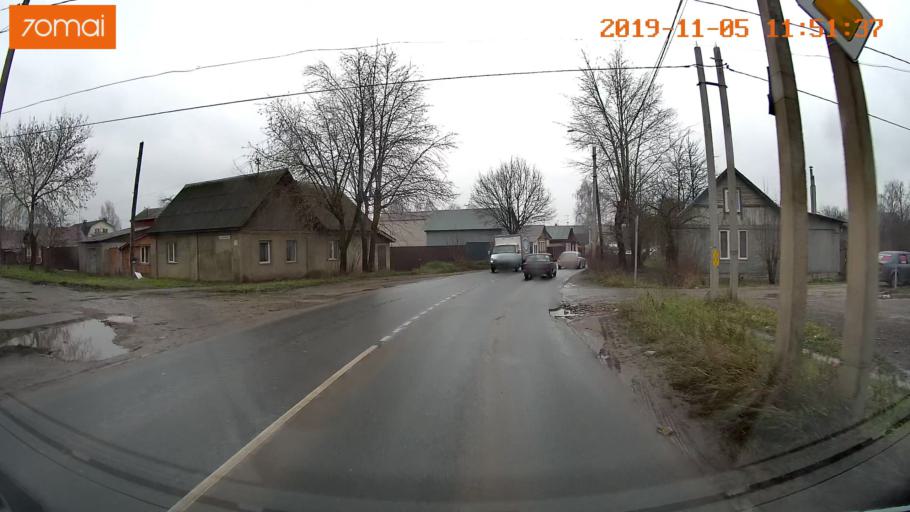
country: RU
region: Ivanovo
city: Bogorodskoye
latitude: 57.0047
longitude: 41.0284
